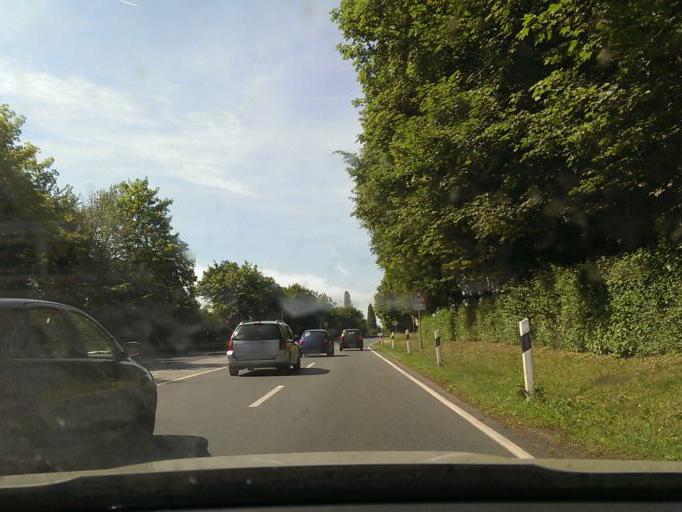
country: DE
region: Lower Saxony
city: Harsum
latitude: 52.1831
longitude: 9.9667
